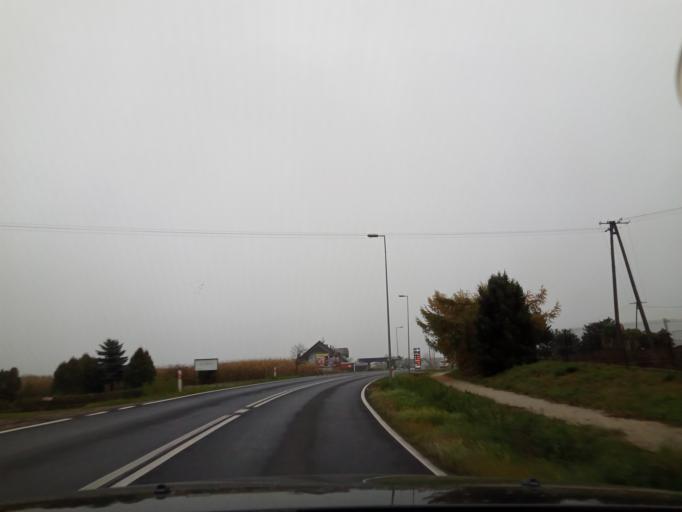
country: PL
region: Lesser Poland Voivodeship
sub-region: Powiat proszowicki
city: Proszowice
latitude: 50.1601
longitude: 20.1923
